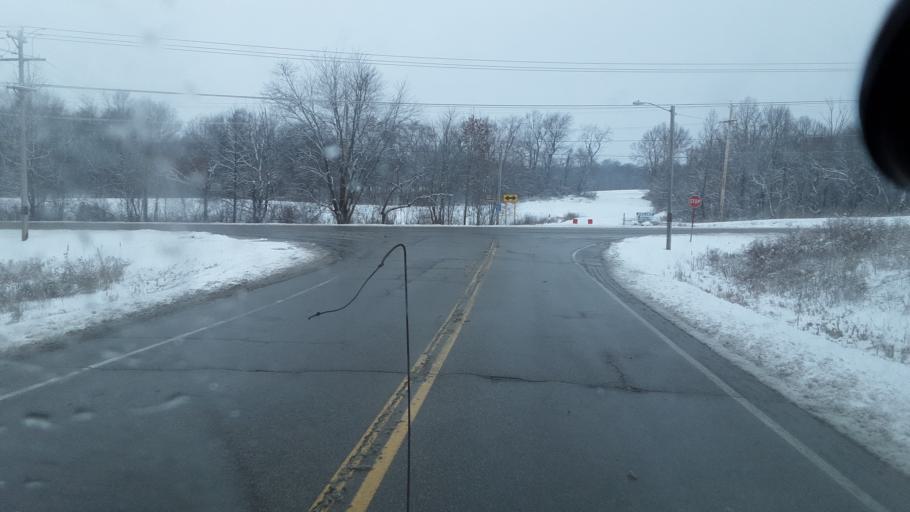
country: US
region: Ohio
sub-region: Licking County
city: Hebron
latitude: 39.9933
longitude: -82.4819
